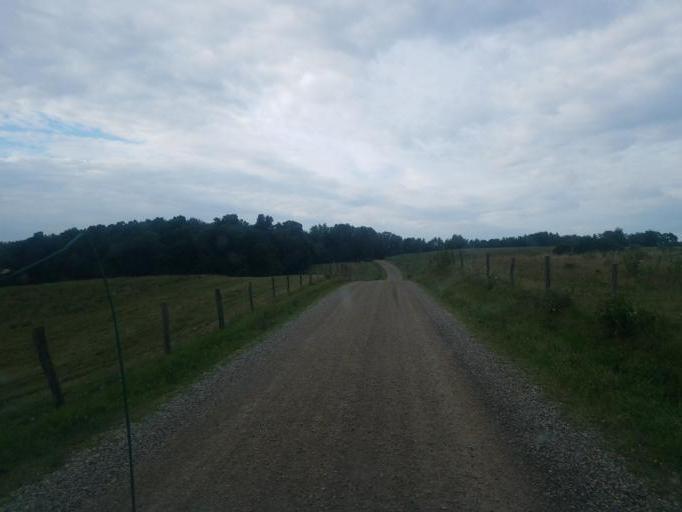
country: US
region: Ohio
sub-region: Knox County
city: Oak Hill
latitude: 40.4136
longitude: -82.1025
